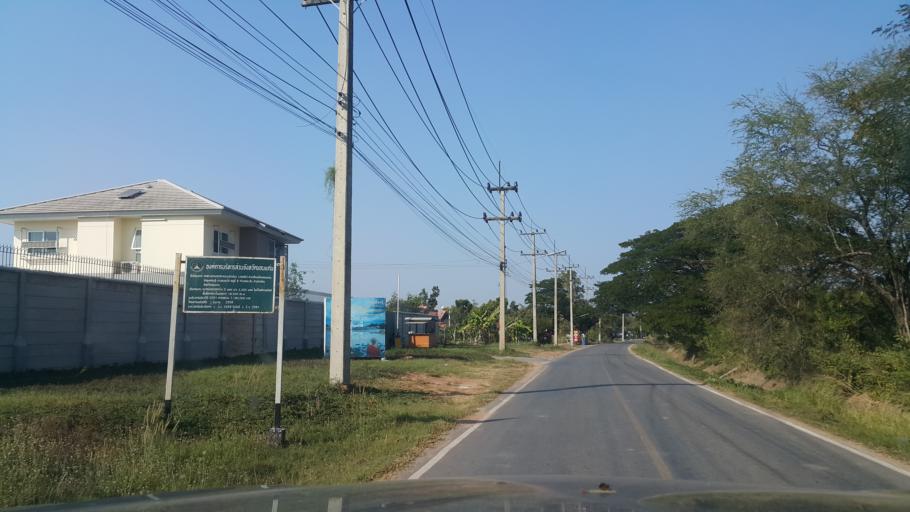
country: TH
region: Khon Kaen
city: Khon Kaen
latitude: 16.4045
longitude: 102.8806
